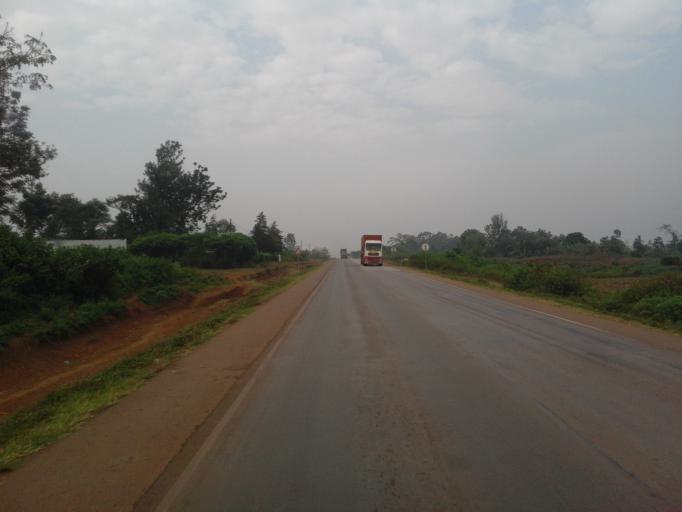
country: UG
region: Eastern Region
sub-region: Busia District
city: Busia
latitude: 0.5801
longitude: 34.0466
